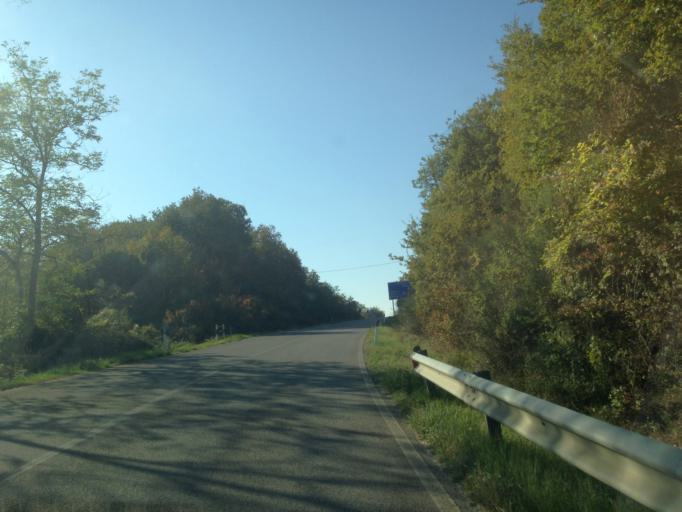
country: IT
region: Tuscany
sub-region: Provincia di Siena
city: Castellina in Chianti
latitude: 43.4789
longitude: 11.2979
